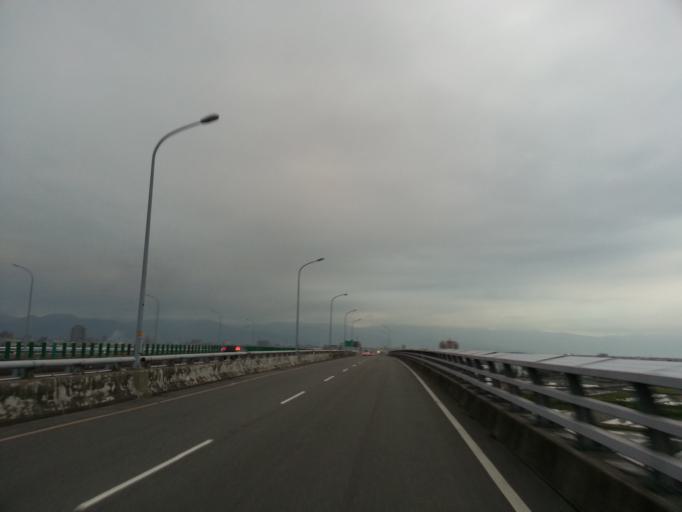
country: TW
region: Taiwan
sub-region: Yilan
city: Yilan
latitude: 24.6595
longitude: 121.8024
